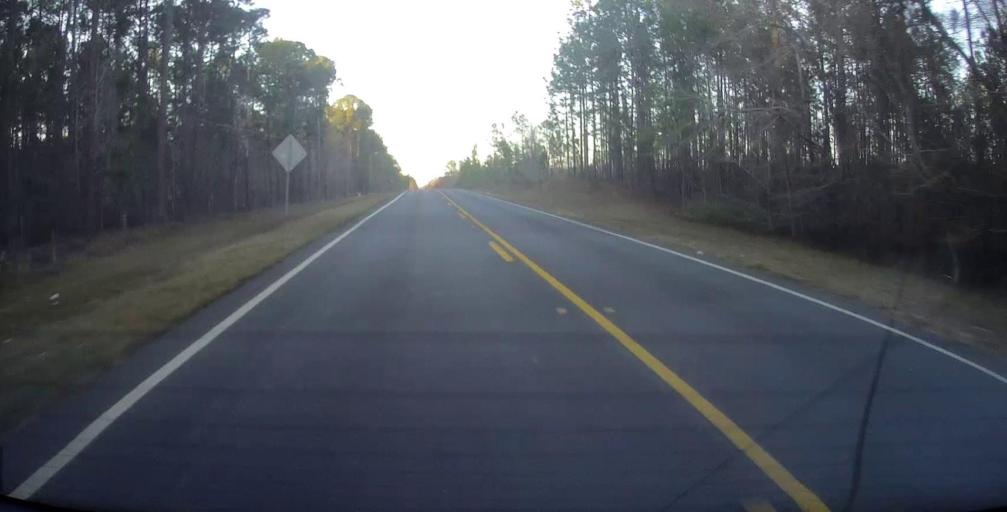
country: US
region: Georgia
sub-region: Dodge County
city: Chester
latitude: 32.3236
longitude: -83.0513
